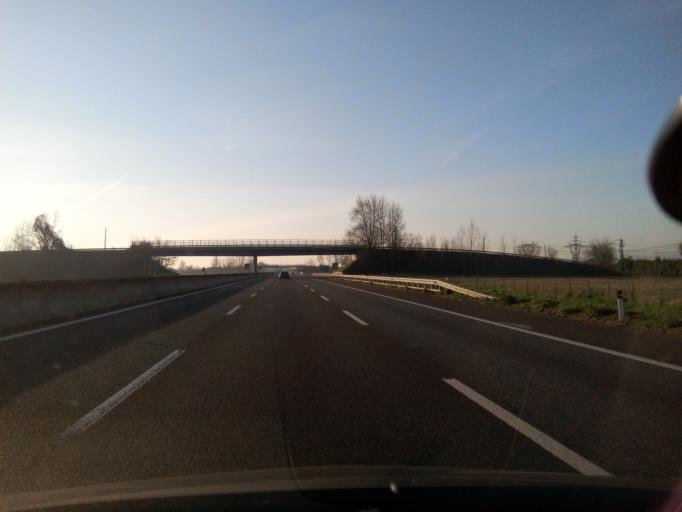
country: IT
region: Lombardy
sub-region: Provincia di Lodi
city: San Rocco al Porto
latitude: 45.0928
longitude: 9.7061
